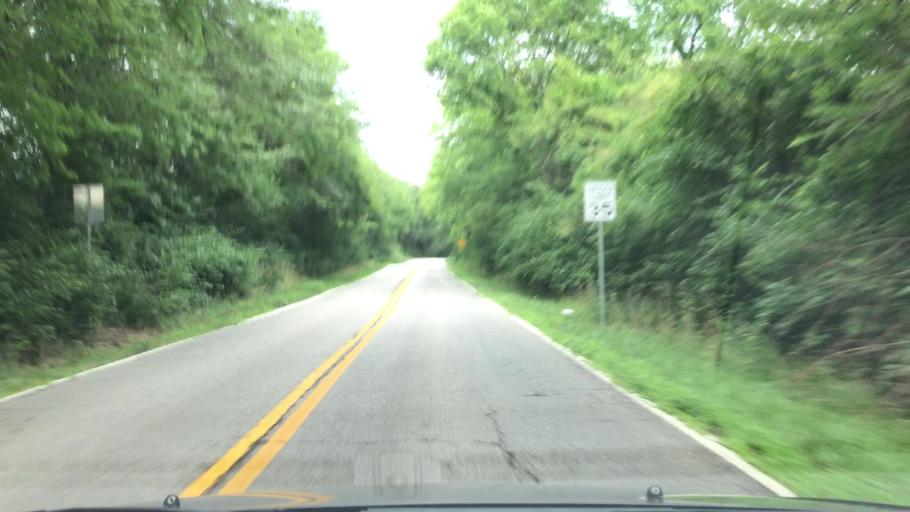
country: US
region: Missouri
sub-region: Jackson County
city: Lees Summit
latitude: 38.8905
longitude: -94.4242
